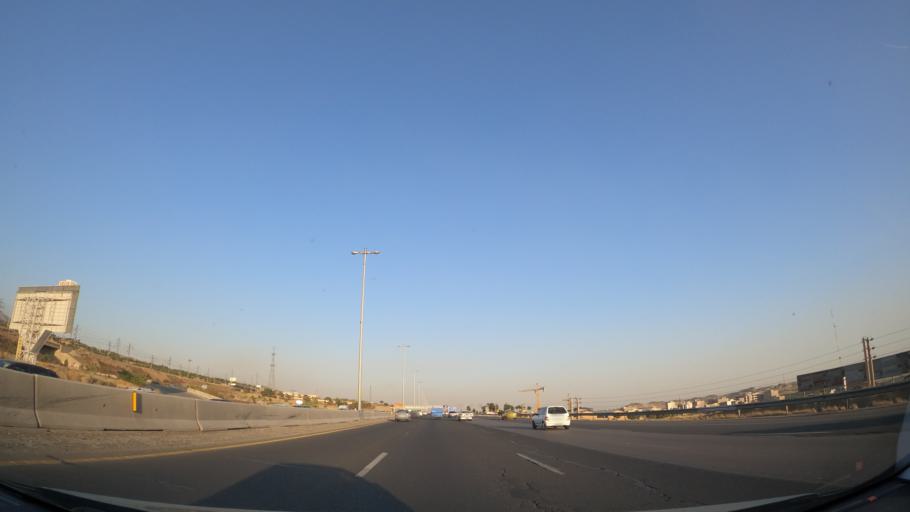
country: IR
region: Tehran
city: Shahr-e Qods
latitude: 35.7530
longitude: 51.0763
